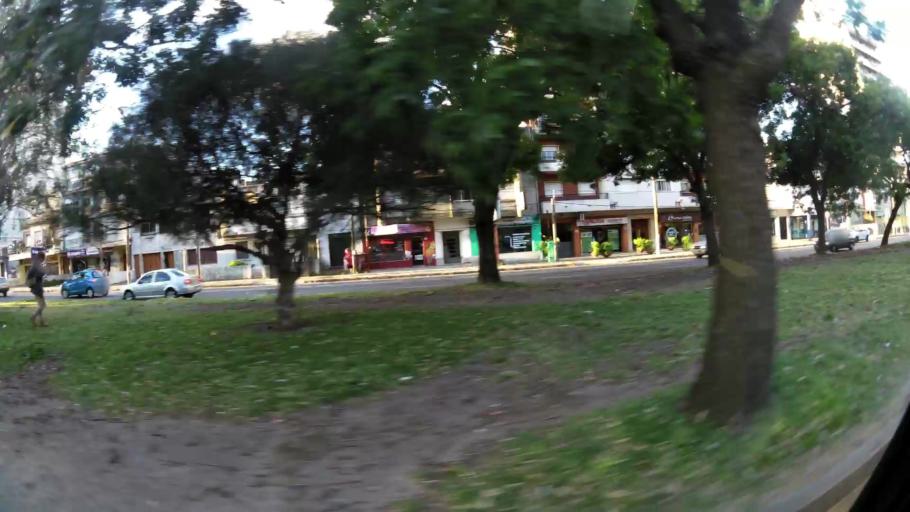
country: UY
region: Montevideo
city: Montevideo
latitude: -34.8909
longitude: -56.1534
